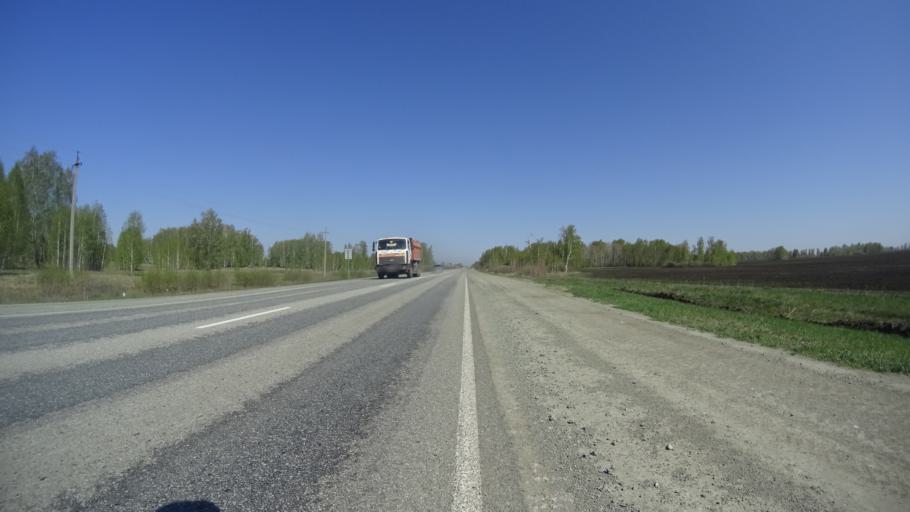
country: RU
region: Chelyabinsk
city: Troitsk
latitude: 54.1814
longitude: 61.4347
